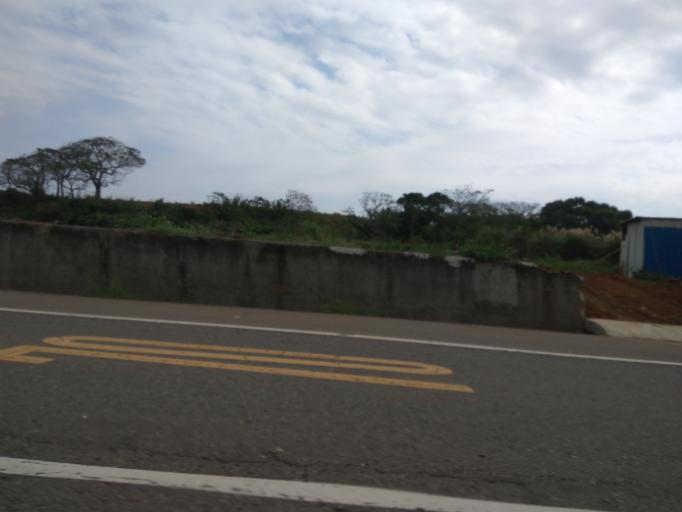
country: TW
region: Taiwan
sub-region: Hsinchu
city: Zhubei
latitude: 24.9614
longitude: 121.0141
